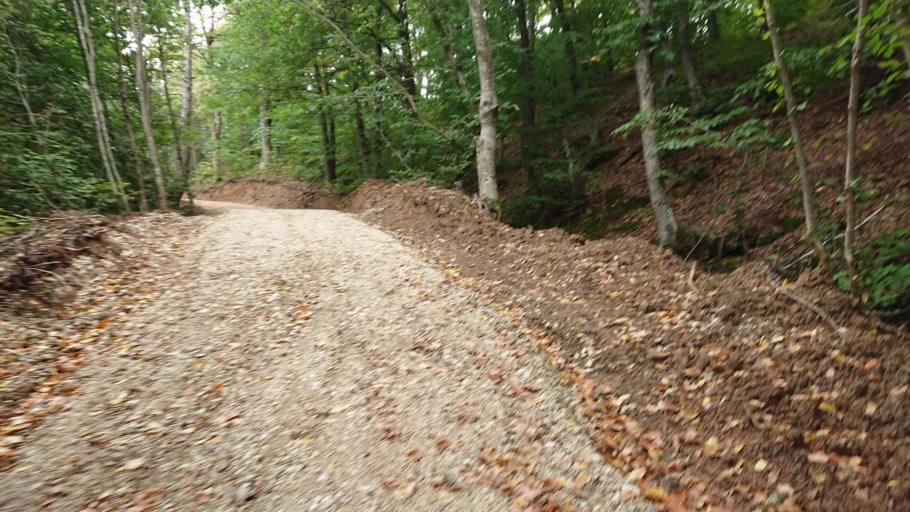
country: TR
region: Bilecik
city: Pazaryeri
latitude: 40.0158
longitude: 29.7940
